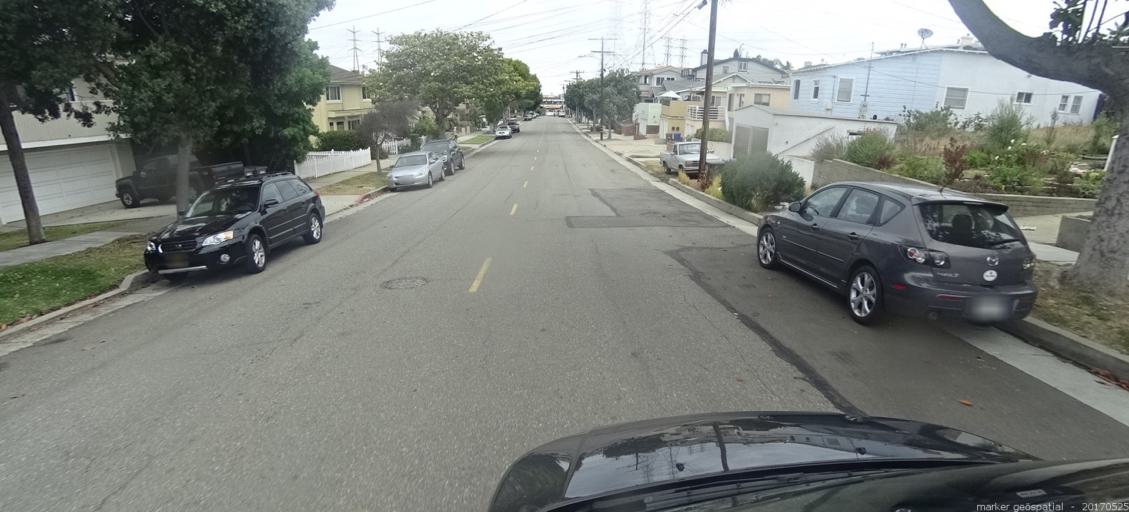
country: US
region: California
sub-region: Los Angeles County
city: Redondo Beach
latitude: 33.8533
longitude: -118.3869
